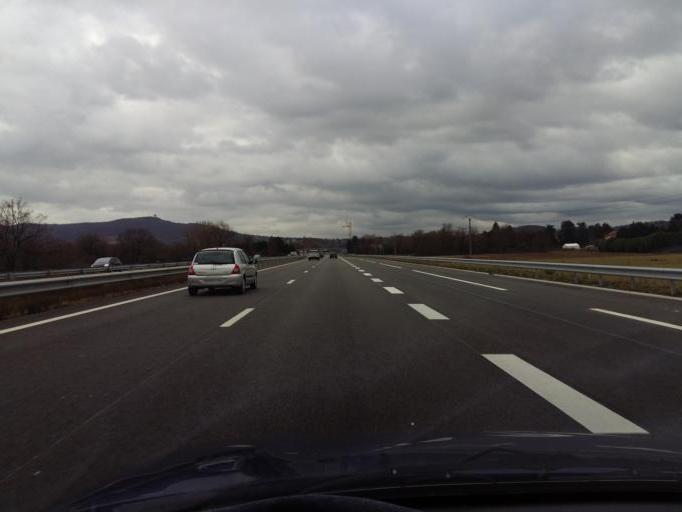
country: FR
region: Rhone-Alpes
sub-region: Departement du Rhone
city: Les Cheres
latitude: 45.8908
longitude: 4.7344
